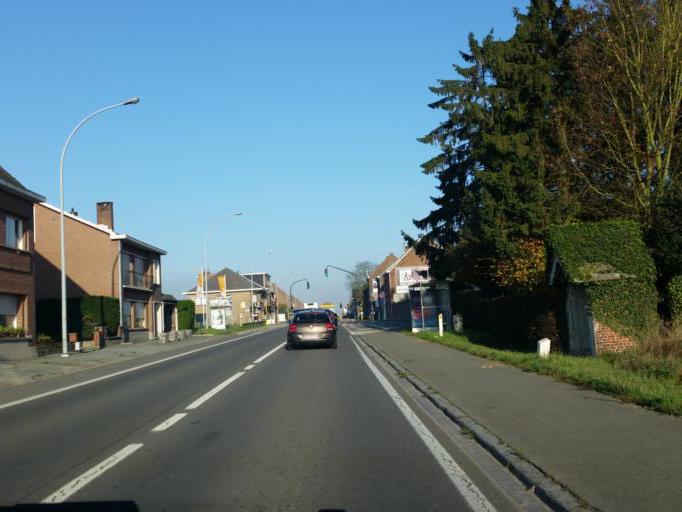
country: BE
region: Flanders
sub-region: Provincie Vlaams-Brabant
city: Opwijk
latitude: 50.9417
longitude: 4.1712
